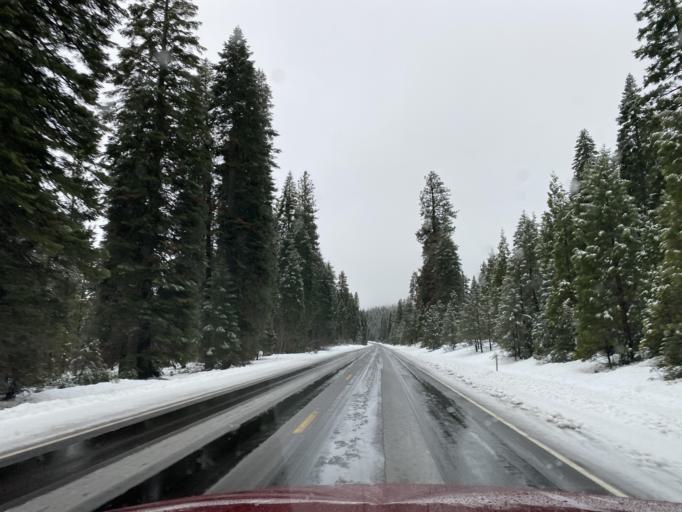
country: US
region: Oregon
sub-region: Klamath County
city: Klamath Falls
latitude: 42.5441
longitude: -122.0879
